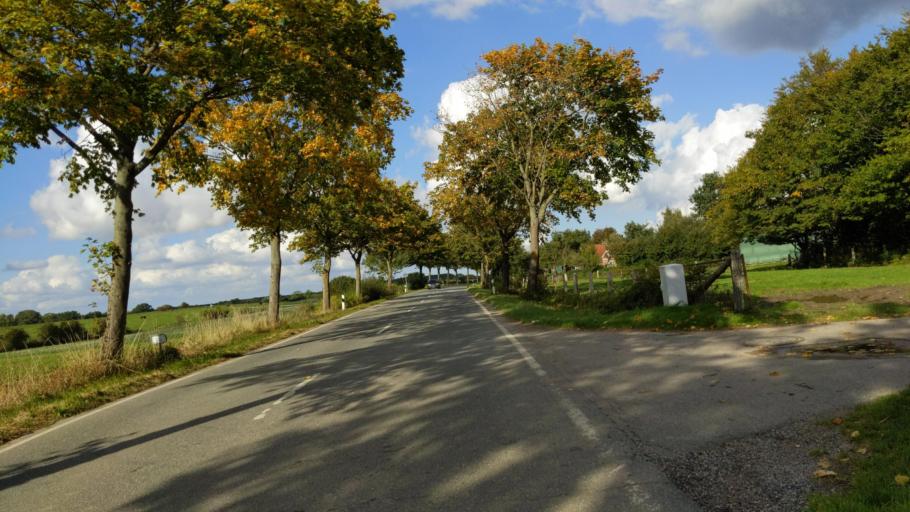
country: DE
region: Schleswig-Holstein
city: Ahrensbok
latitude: 54.0142
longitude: 10.5856
